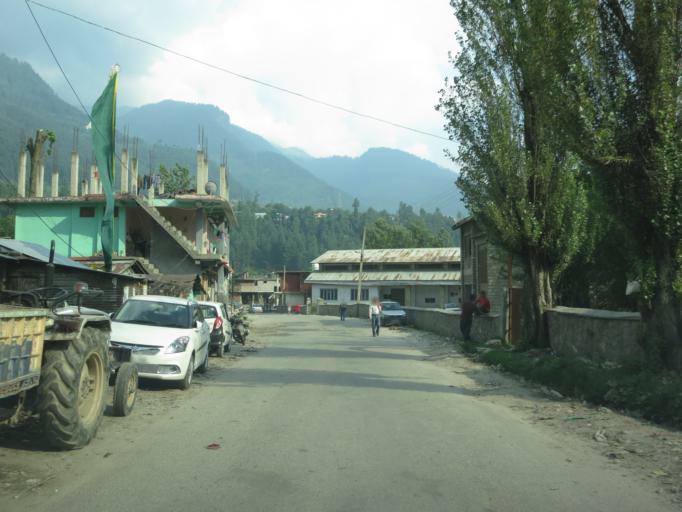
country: IN
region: Himachal Pradesh
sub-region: Kulu
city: Nagar
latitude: 32.1117
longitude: 77.1482
